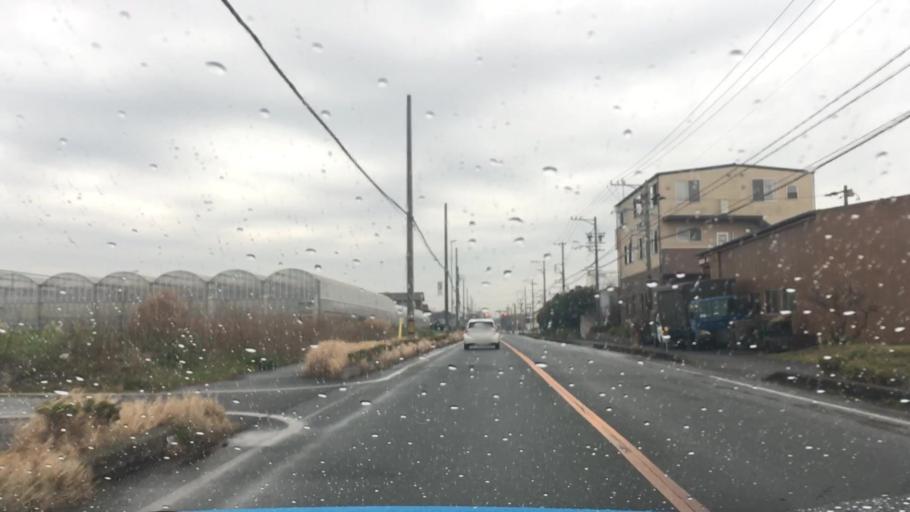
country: JP
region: Aichi
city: Toyohashi
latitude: 34.6925
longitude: 137.3906
